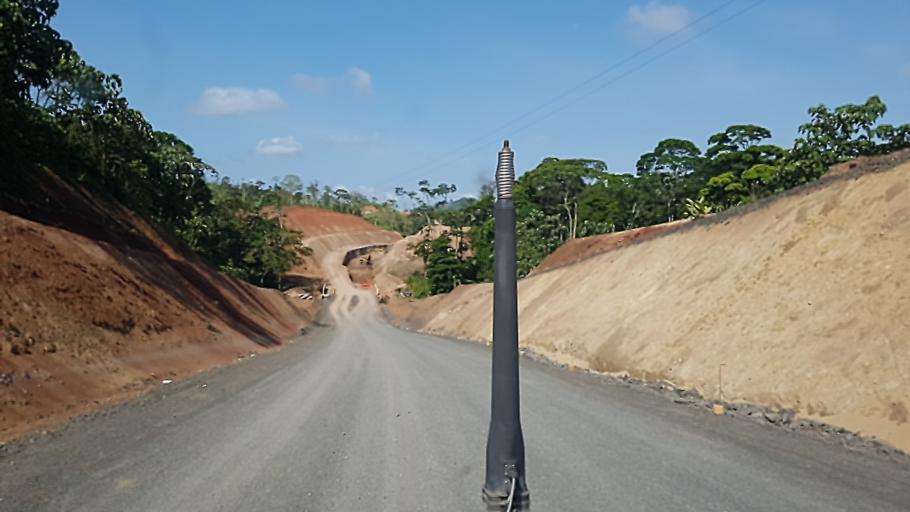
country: NI
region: Atlantico Sur
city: Nueva Guinea
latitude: 11.8050
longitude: -84.1212
